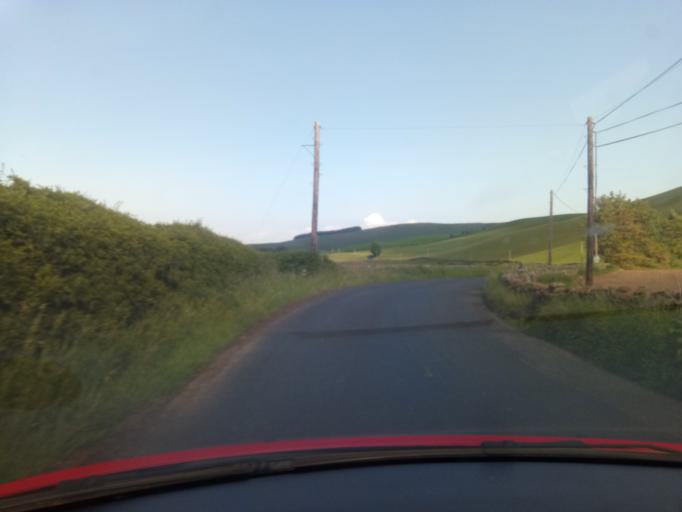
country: GB
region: Scotland
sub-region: The Scottish Borders
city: Selkirk
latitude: 55.5104
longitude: -2.9547
